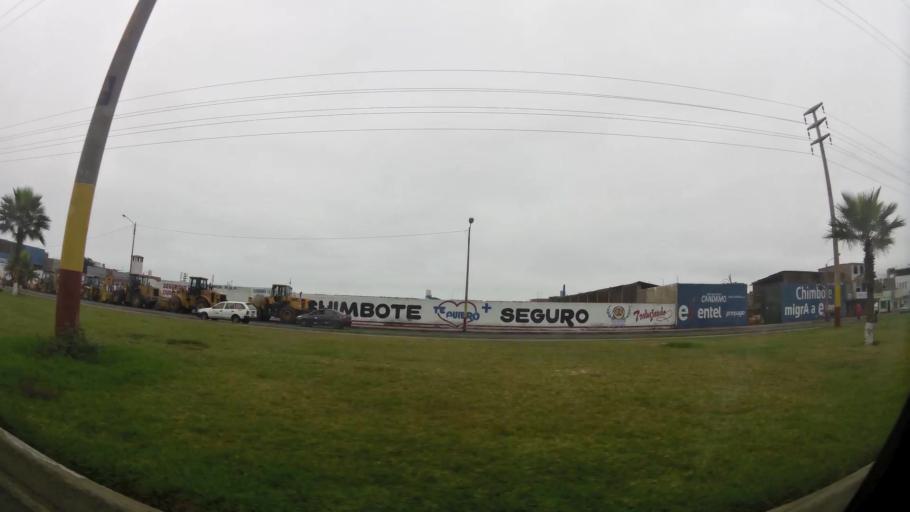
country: PE
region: Ancash
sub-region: Provincia de Santa
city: Chimbote
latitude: -9.0830
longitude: -78.5756
